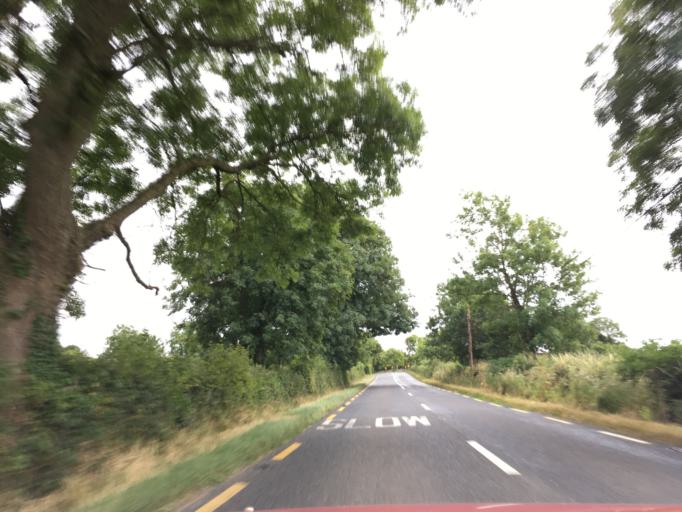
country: IE
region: Munster
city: Fethard
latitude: 52.4334
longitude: -7.7869
